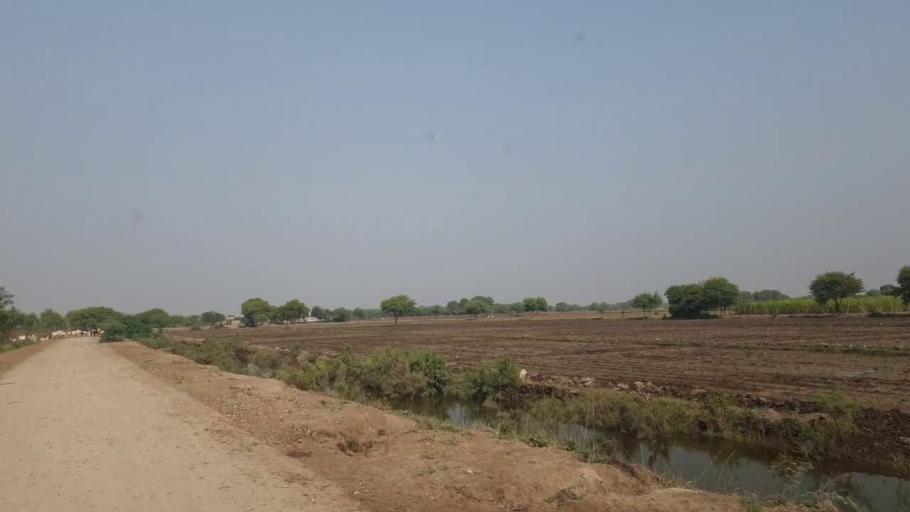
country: PK
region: Sindh
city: Matli
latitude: 25.1492
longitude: 68.7016
